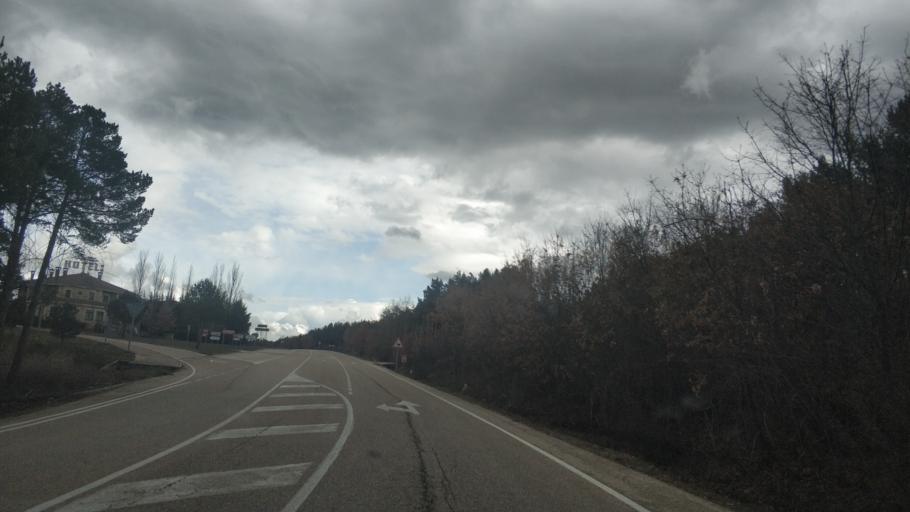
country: ES
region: Castille and Leon
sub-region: Provincia de Burgos
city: Quintanar de la Sierra
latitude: 41.9711
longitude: -3.0401
